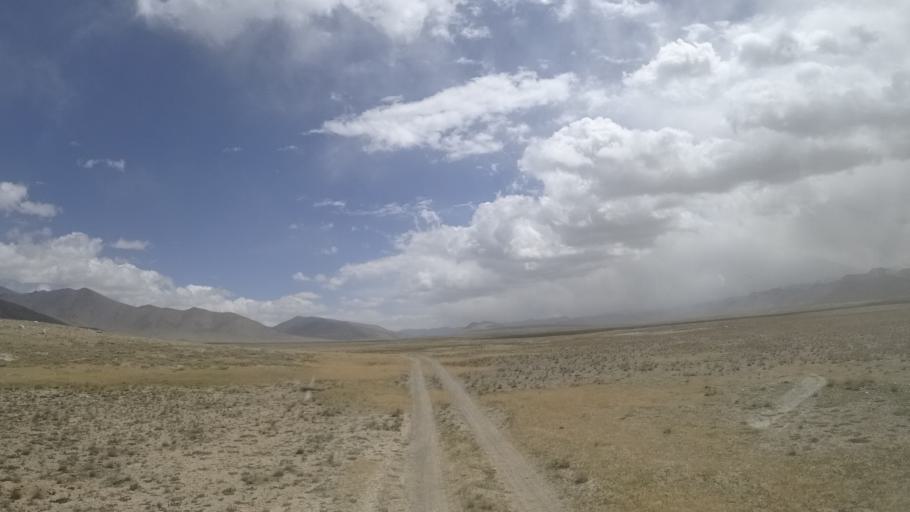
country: TJ
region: Gorno-Badakhshan
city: Murghob
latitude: 37.4735
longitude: 73.9711
